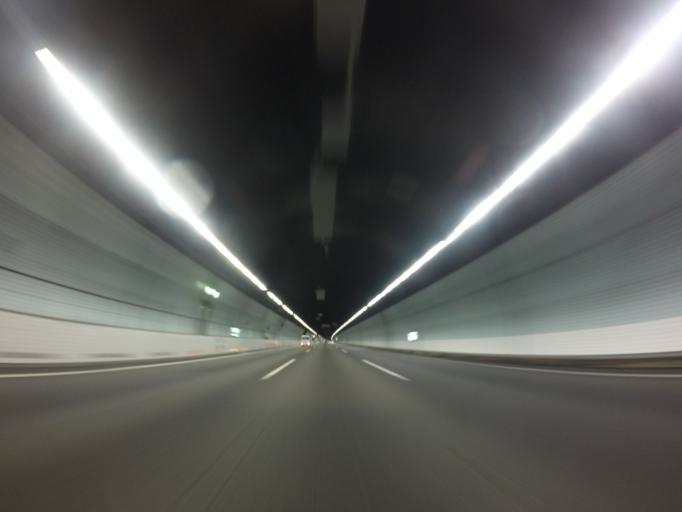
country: JP
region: Shizuoka
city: Yaizu
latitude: 34.9053
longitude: 138.3390
